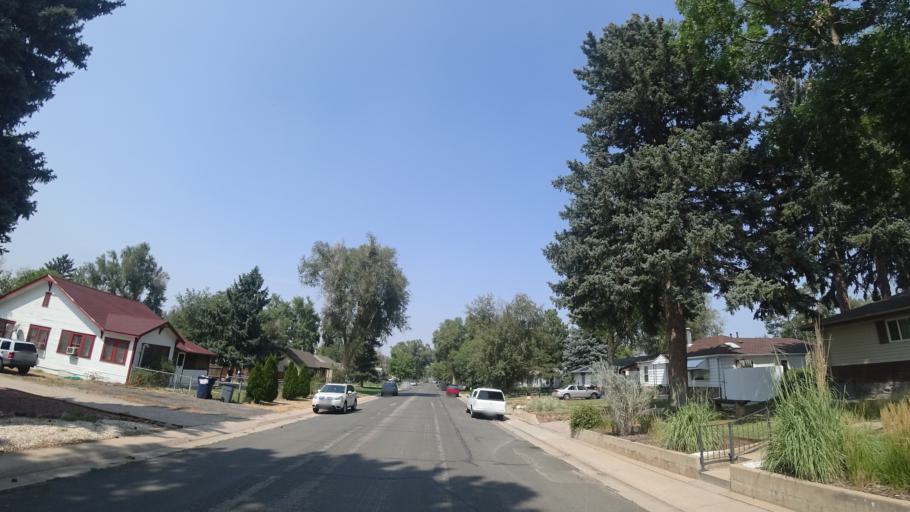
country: US
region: Colorado
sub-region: Arapahoe County
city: Englewood
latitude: 39.6389
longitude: -104.9948
